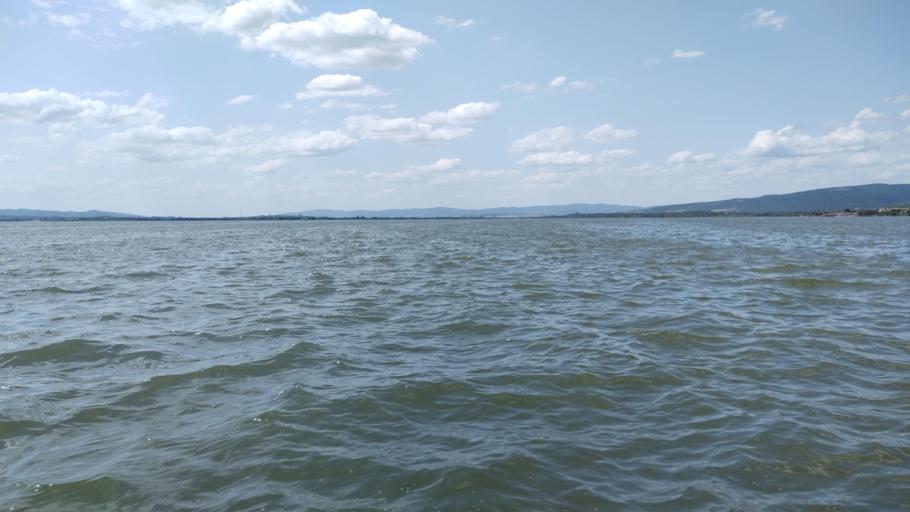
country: RO
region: Caras-Severin
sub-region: Comuna Pescari
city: Coronini
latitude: 44.6722
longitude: 21.6770
